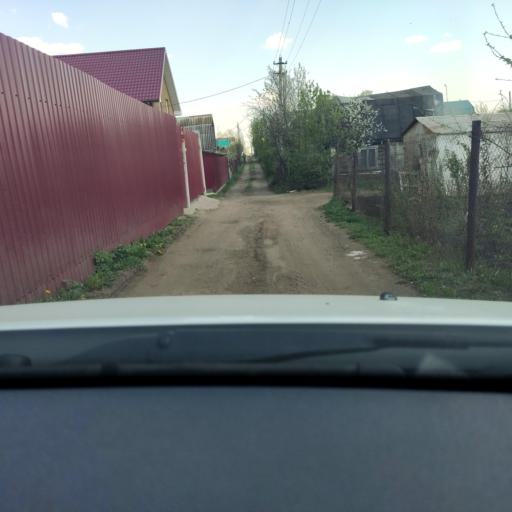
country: RU
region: Bashkortostan
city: Mikhaylovka
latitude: 54.8344
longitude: 55.9530
